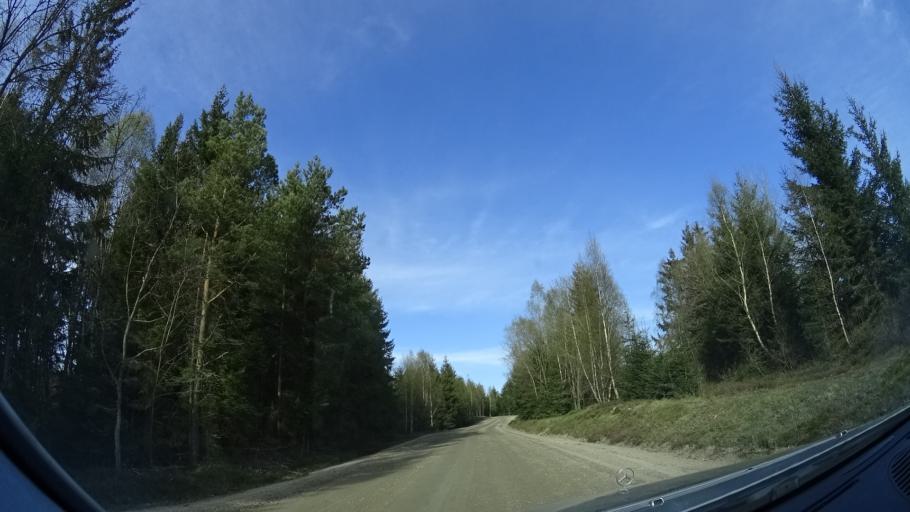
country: SE
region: Skane
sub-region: Hassleholms Kommun
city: Sosdala
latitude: 56.0867
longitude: 13.6787
